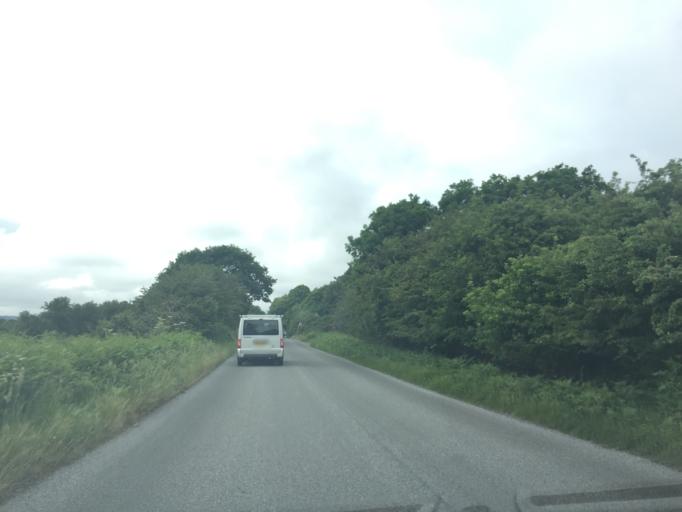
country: GB
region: England
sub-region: Dorset
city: Wareham
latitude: 50.6822
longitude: -2.1489
